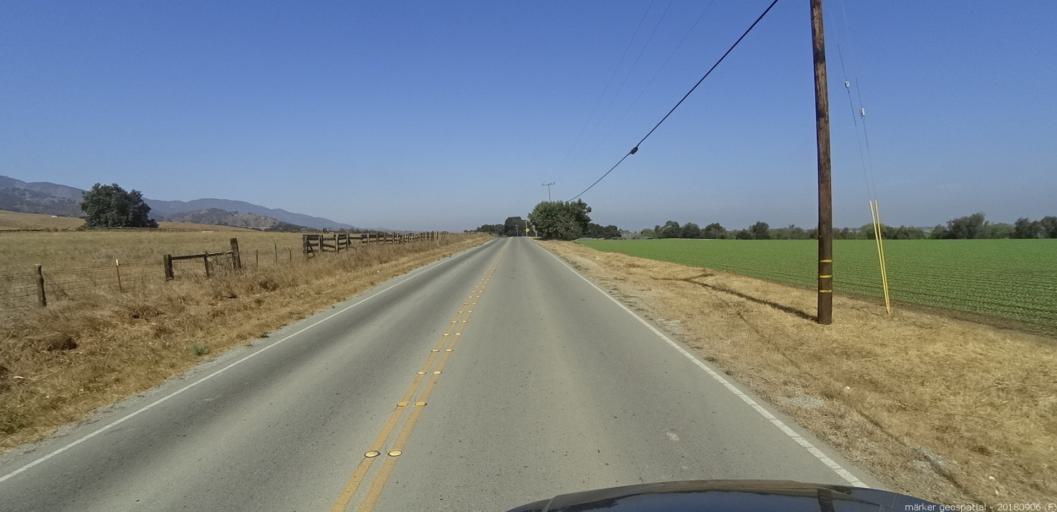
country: US
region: California
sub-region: Monterey County
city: Chualar
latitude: 36.5707
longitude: -121.5714
